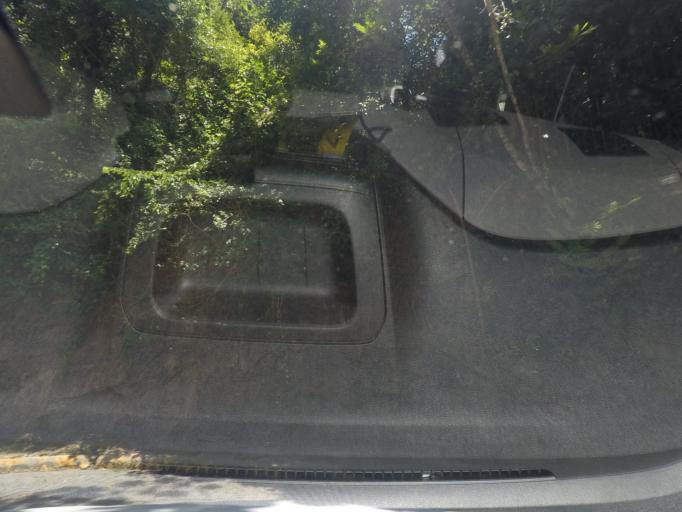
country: BR
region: Rio de Janeiro
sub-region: Rio De Janeiro
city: Rio de Janeiro
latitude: -22.9635
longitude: -43.1835
